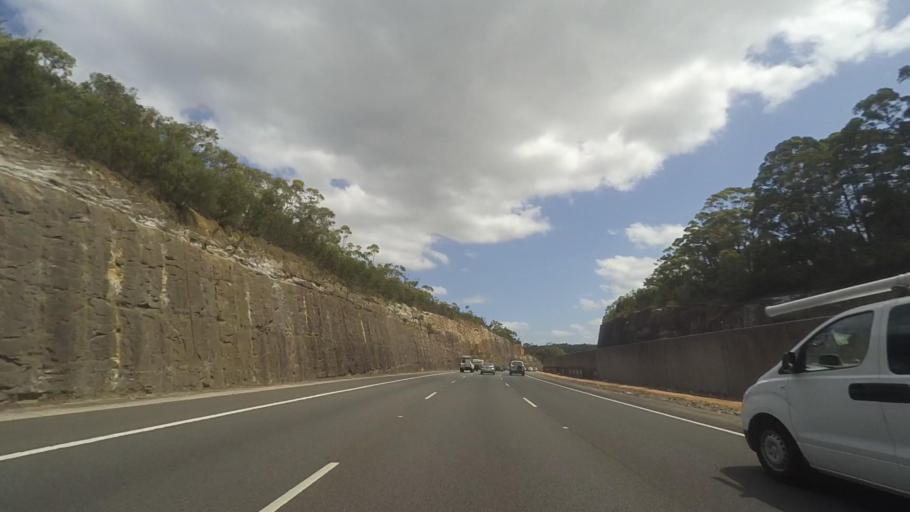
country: AU
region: New South Wales
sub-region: Hornsby Shire
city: Berowra
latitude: -33.5964
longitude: 151.1727
